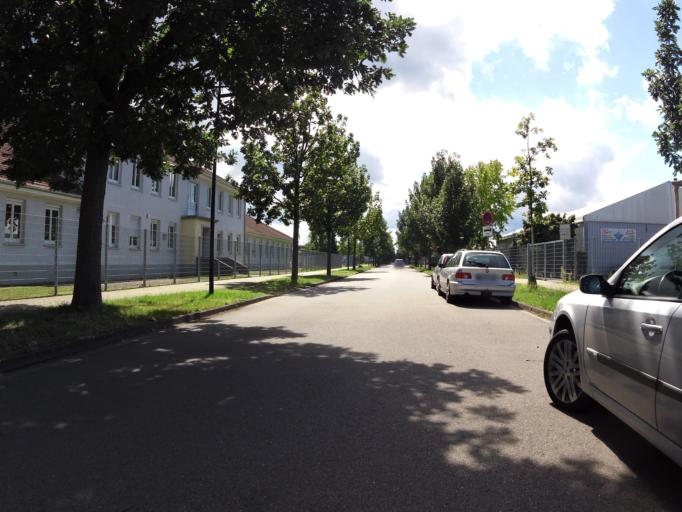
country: DE
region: Baden-Wuerttemberg
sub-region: Freiburg Region
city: Lahr
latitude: 48.3519
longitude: 7.8270
